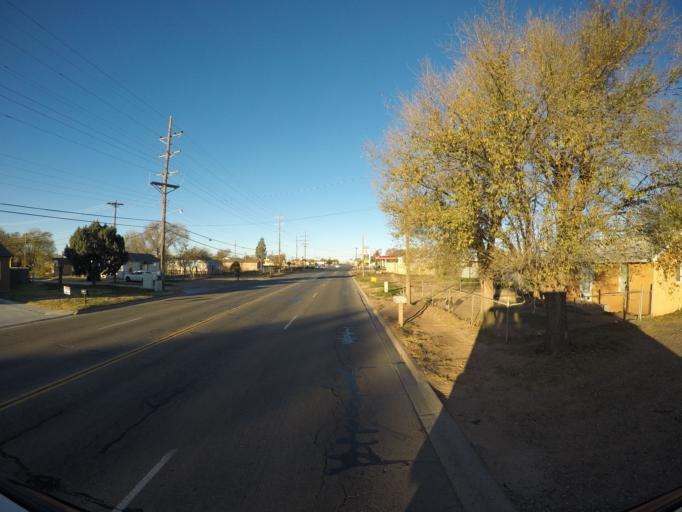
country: US
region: New Mexico
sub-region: Curry County
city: Clovis
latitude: 34.3903
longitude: -103.1944
